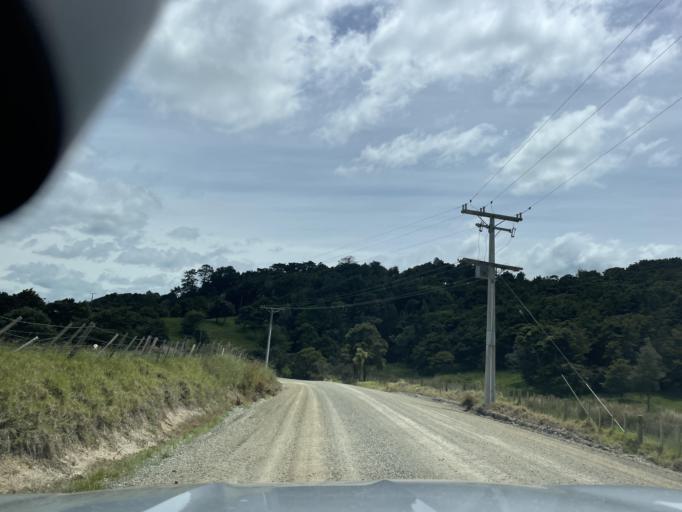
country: NZ
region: Auckland
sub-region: Auckland
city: Wellsford
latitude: -36.1532
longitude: 174.2873
